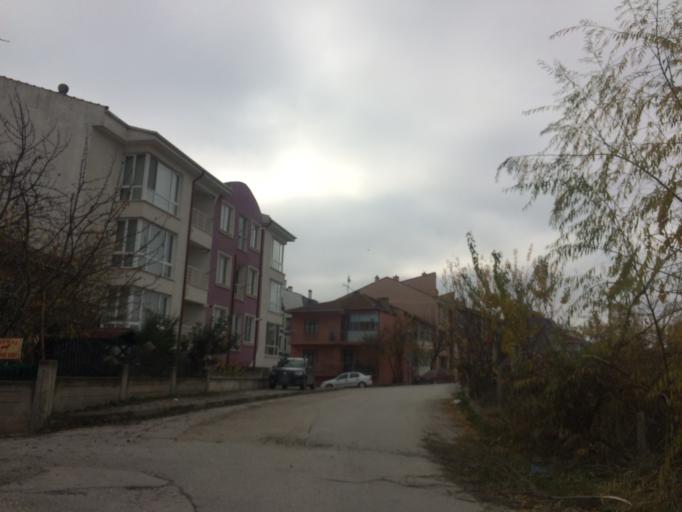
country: TR
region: Eskisehir
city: Eskisehir
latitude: 39.7788
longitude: 30.4777
